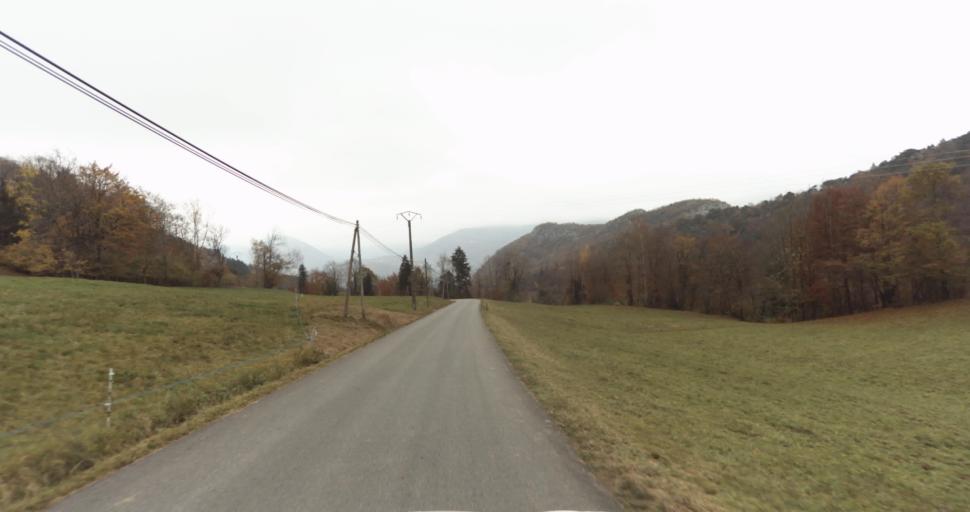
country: FR
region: Rhone-Alpes
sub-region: Departement de la Haute-Savoie
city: Saint-Jorioz
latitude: 45.8072
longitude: 6.1922
